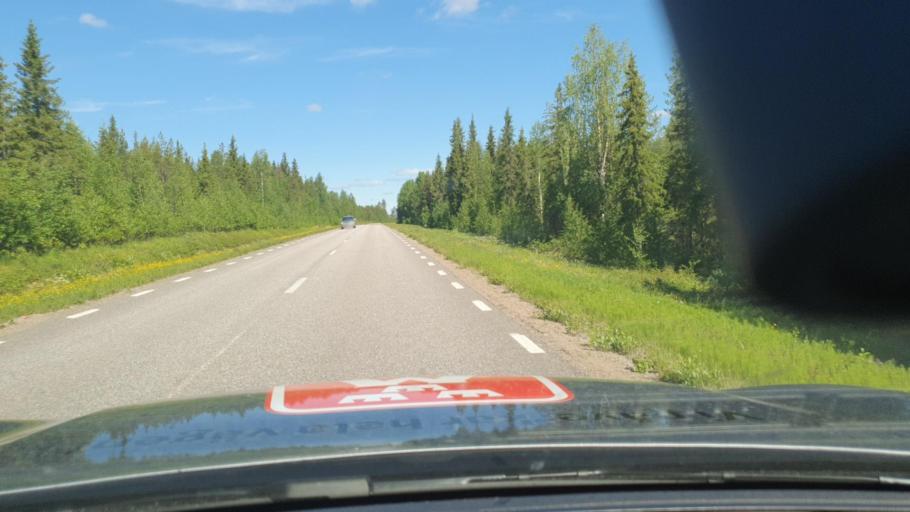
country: SE
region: Norrbotten
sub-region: Overkalix Kommun
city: OEverkalix
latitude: 66.6805
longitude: 22.6812
